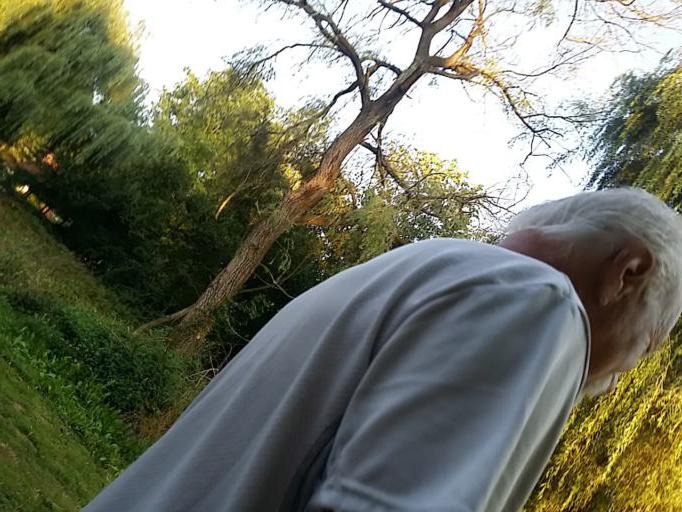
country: HU
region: Baranya
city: Pellerd
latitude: 46.1393
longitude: 18.1133
